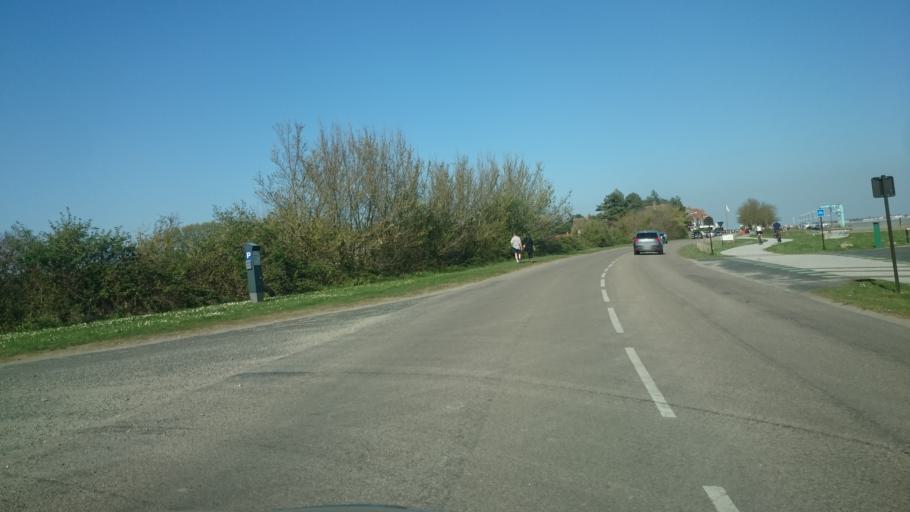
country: FR
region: Picardie
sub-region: Departement de la Somme
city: Pende
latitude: 50.2130
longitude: 1.5602
